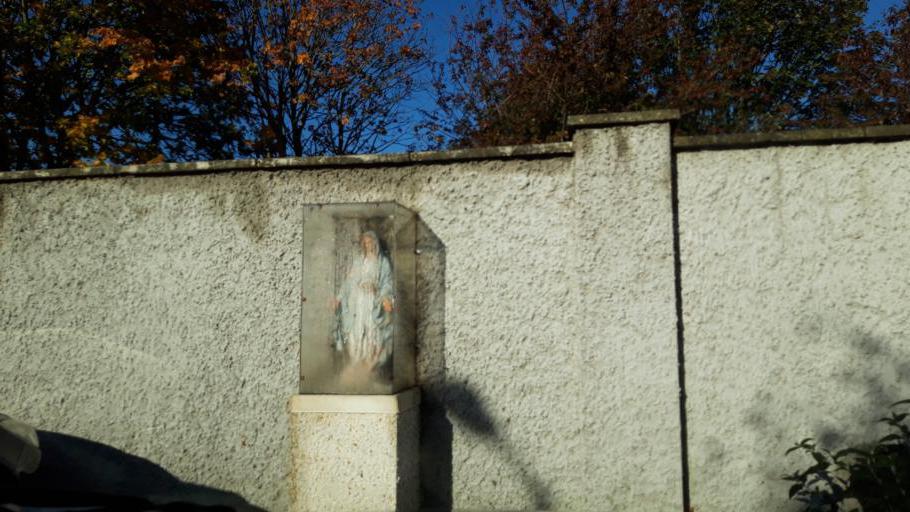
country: IE
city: Coolock
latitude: 53.3858
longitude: -6.1909
